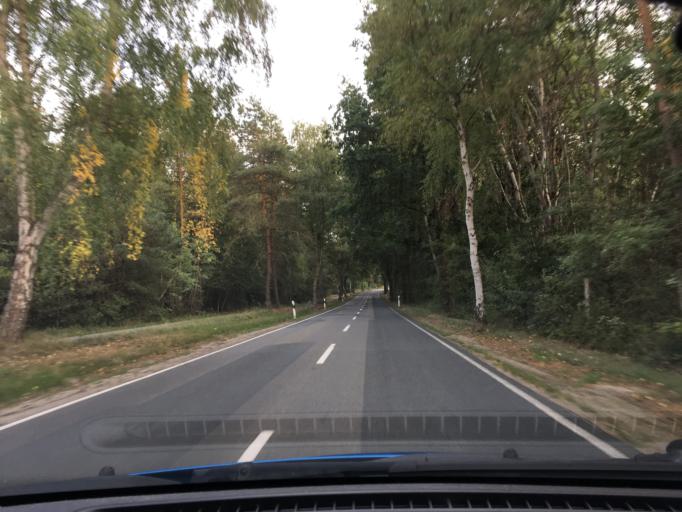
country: DE
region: Lower Saxony
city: Vierhofen
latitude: 53.2506
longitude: 10.2291
